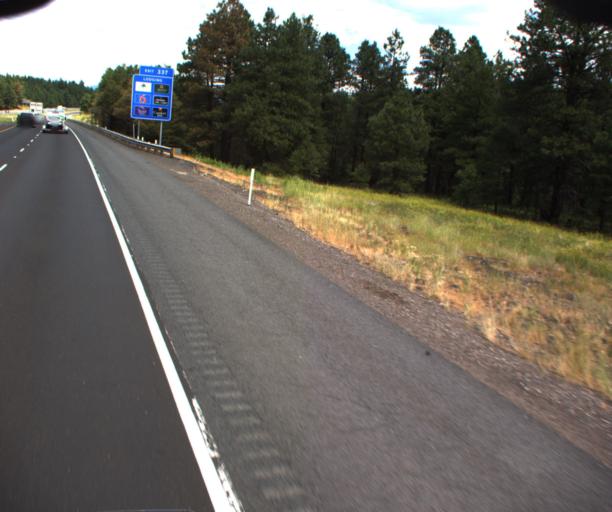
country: US
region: Arizona
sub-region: Coconino County
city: Kachina Village
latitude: 35.1073
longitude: -111.6810
